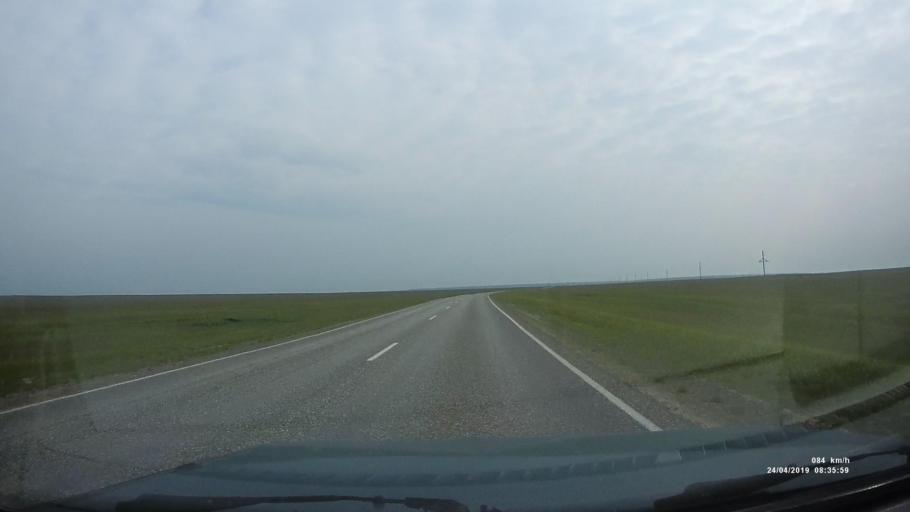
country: RU
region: Kalmykiya
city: Arshan'
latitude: 46.2018
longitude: 43.9270
